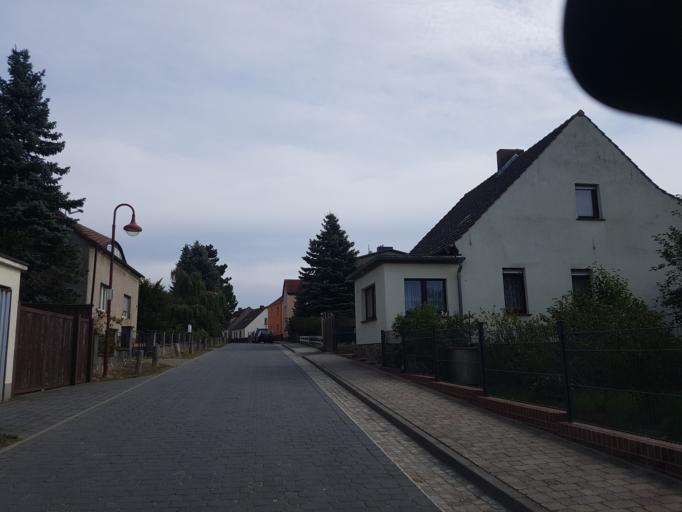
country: DE
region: Brandenburg
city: Wiesenburg
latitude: 52.1157
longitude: 12.4481
